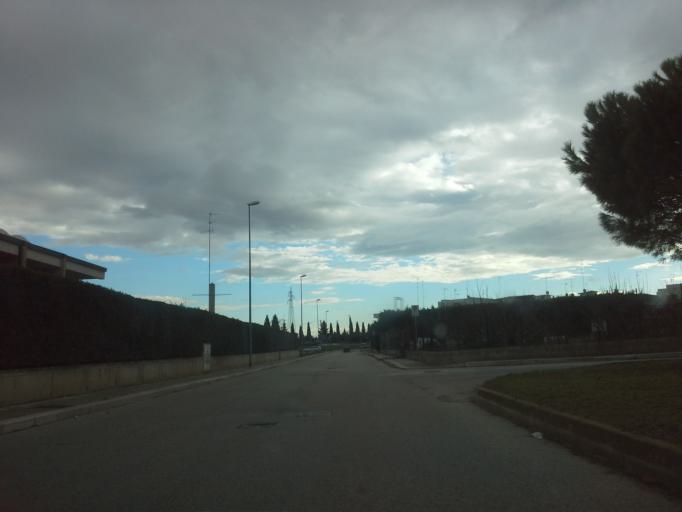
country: IT
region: Apulia
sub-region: Provincia di Bari
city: Adelfia
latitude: 41.0055
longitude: 16.8810
